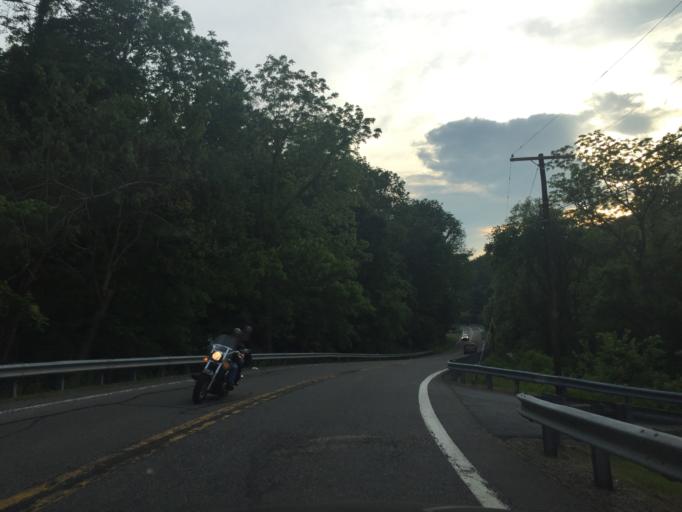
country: US
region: Maryland
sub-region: Frederick County
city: Brunswick
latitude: 39.3282
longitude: -77.6598
